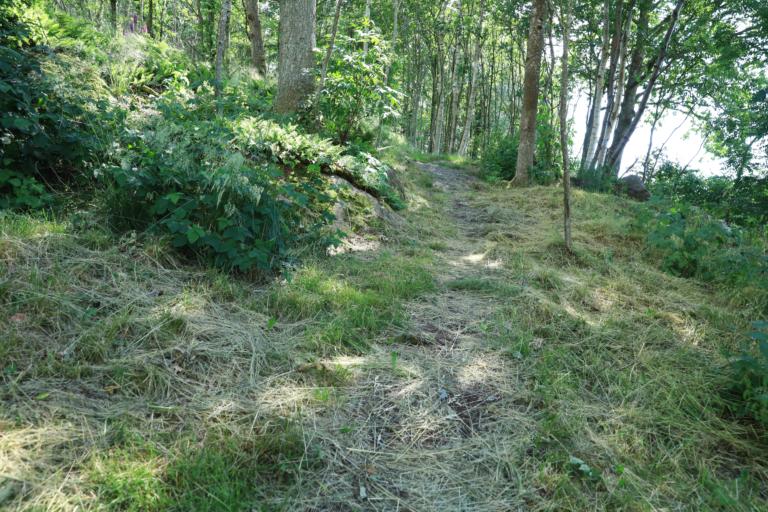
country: SE
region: Halland
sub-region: Varbergs Kommun
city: Varberg
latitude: 57.1722
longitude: 12.2922
